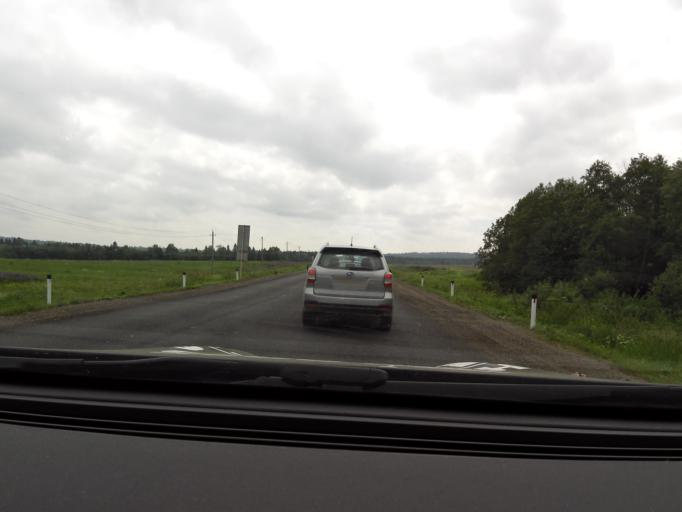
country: RU
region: Perm
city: Zvezdnyy
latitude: 57.7789
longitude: 56.3458
